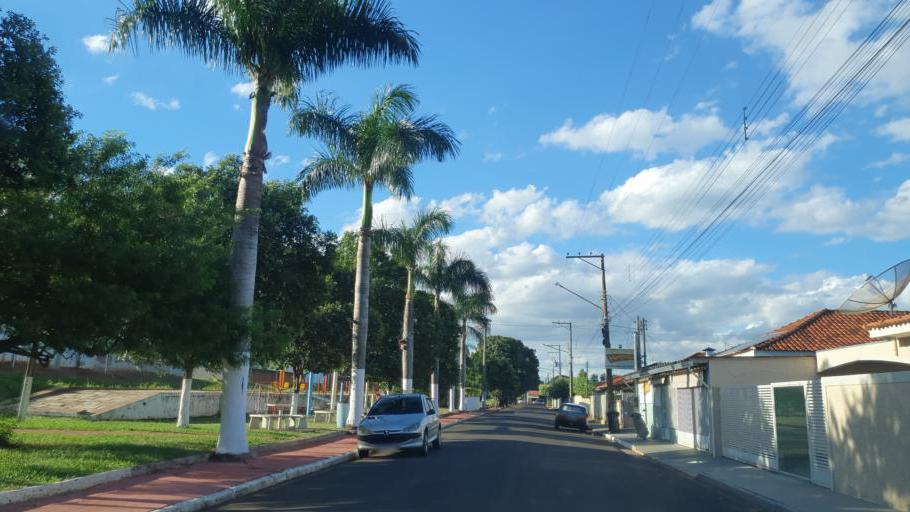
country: BR
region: Sao Paulo
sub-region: Quata
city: Quata
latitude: -22.2527
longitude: -50.7663
